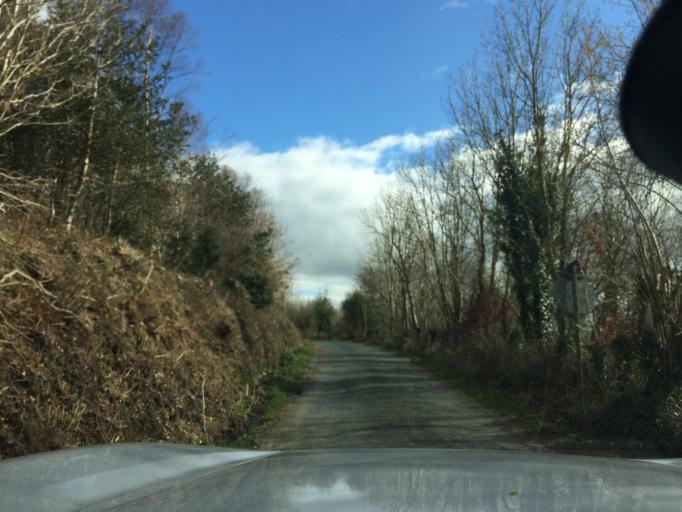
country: IE
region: Munster
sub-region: Waterford
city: Portlaw
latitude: 52.2788
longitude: -7.3695
